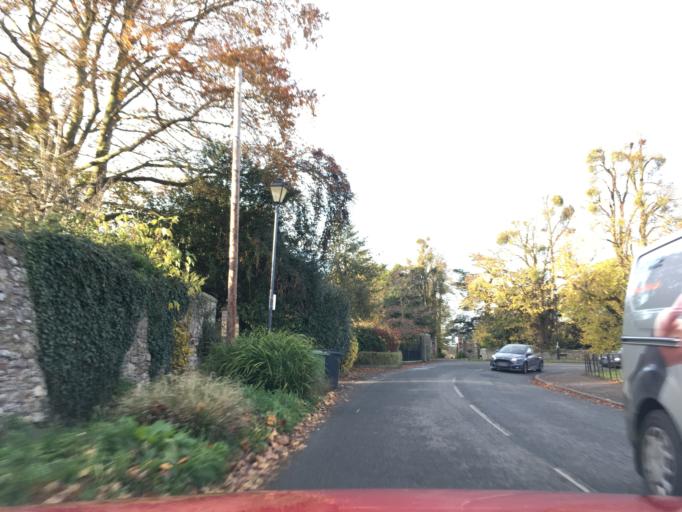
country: GB
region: England
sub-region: South Gloucestershire
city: Thornbury
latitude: 51.6123
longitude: -2.5302
